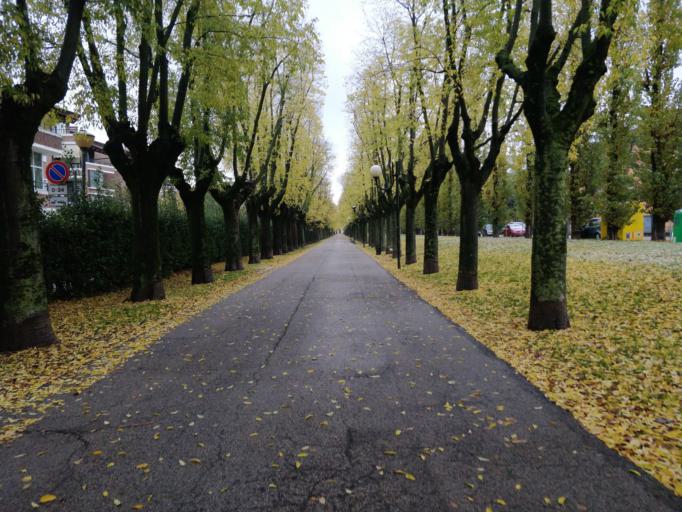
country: IT
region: Emilia-Romagna
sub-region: Provincia di Ferrara
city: Cento
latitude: 44.7300
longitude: 11.2936
